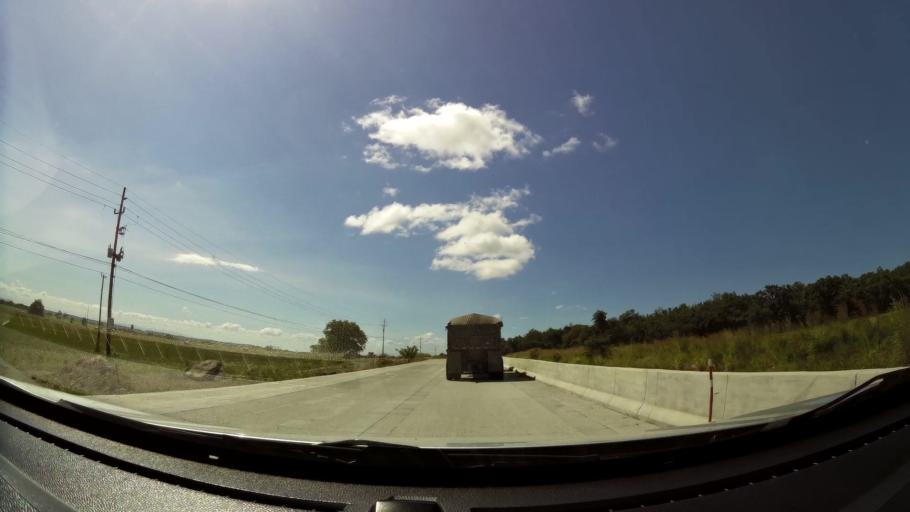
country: CR
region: Guanacaste
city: Bagaces
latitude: 10.5397
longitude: -85.3239
